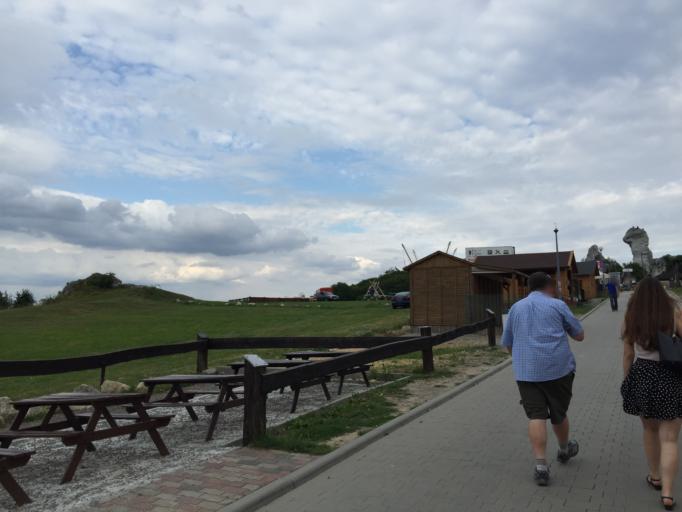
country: PL
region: Silesian Voivodeship
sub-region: Powiat zawiercianski
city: Ogrodzieniec
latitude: 50.4539
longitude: 19.5502
